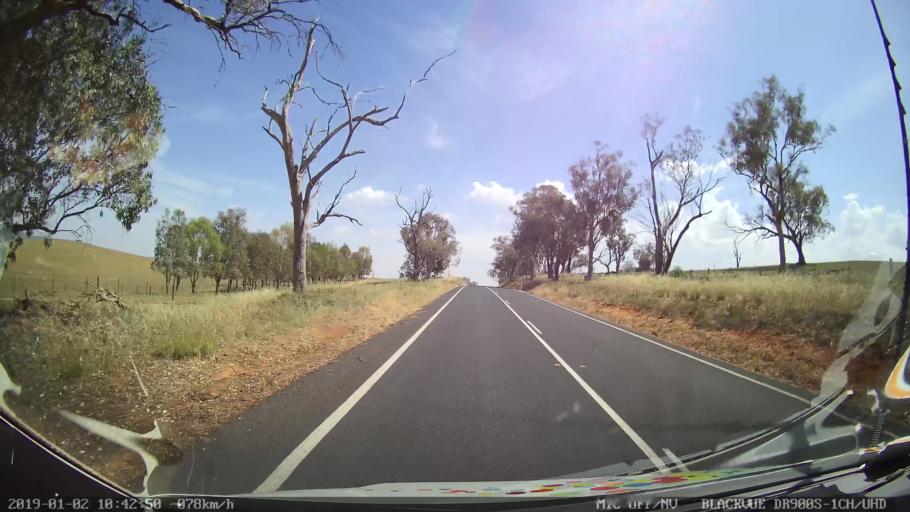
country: AU
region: New South Wales
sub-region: Cootamundra
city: Cootamundra
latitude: -34.7795
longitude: 148.3064
